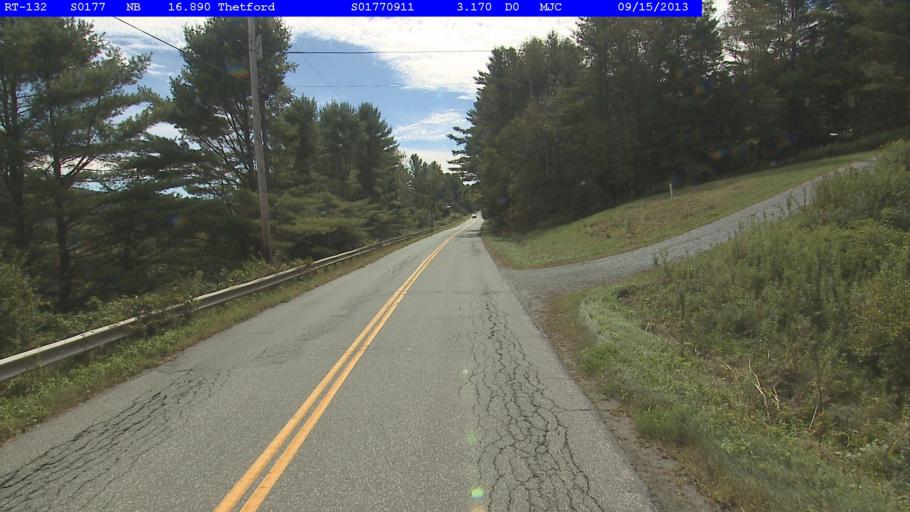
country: US
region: New Hampshire
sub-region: Grafton County
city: Hanover
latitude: 43.8127
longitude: -72.2743
